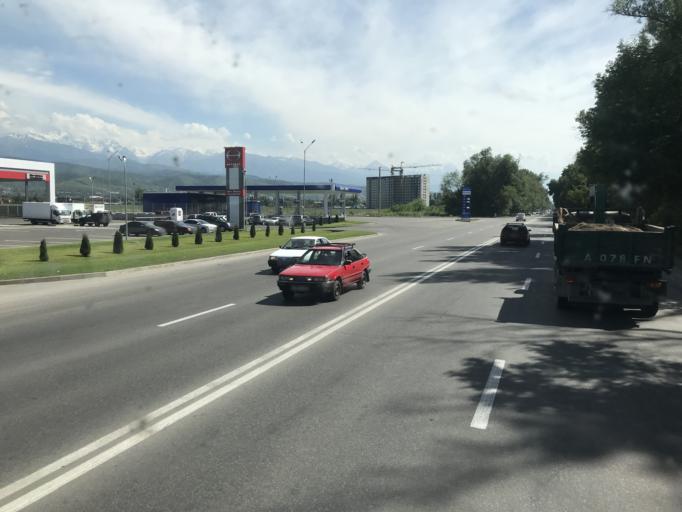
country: KZ
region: Almaty Oblysy
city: Energeticheskiy
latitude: 43.3291
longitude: 77.0335
